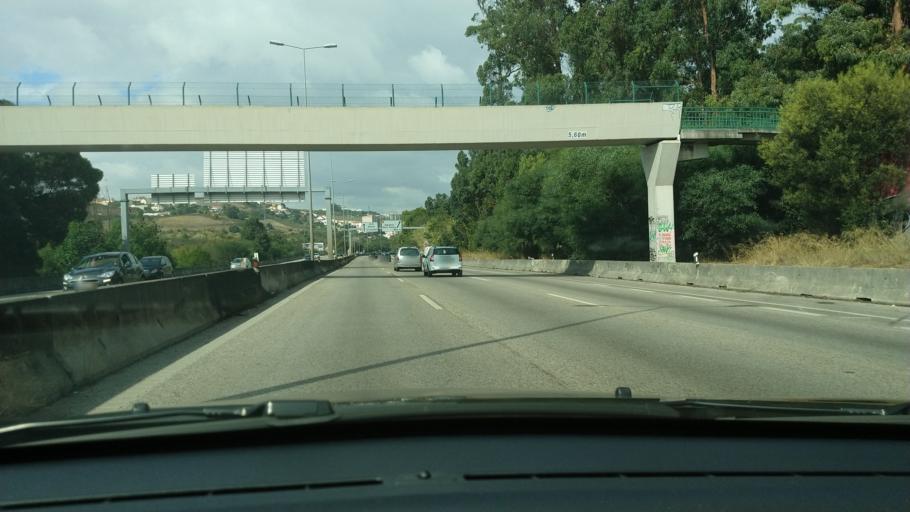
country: PT
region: Lisbon
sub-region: Sintra
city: Cacem
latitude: 38.7512
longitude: -9.2870
